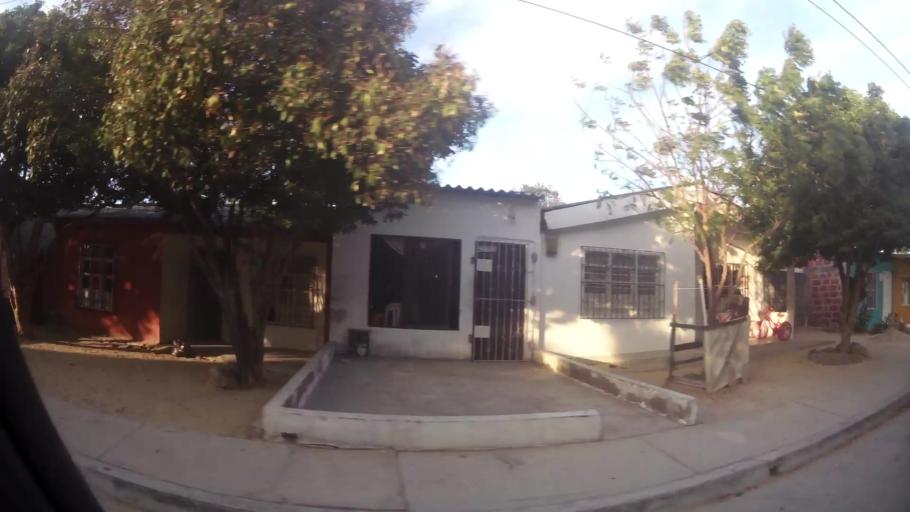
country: CO
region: Atlantico
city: Barranquilla
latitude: 10.9594
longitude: -74.8234
